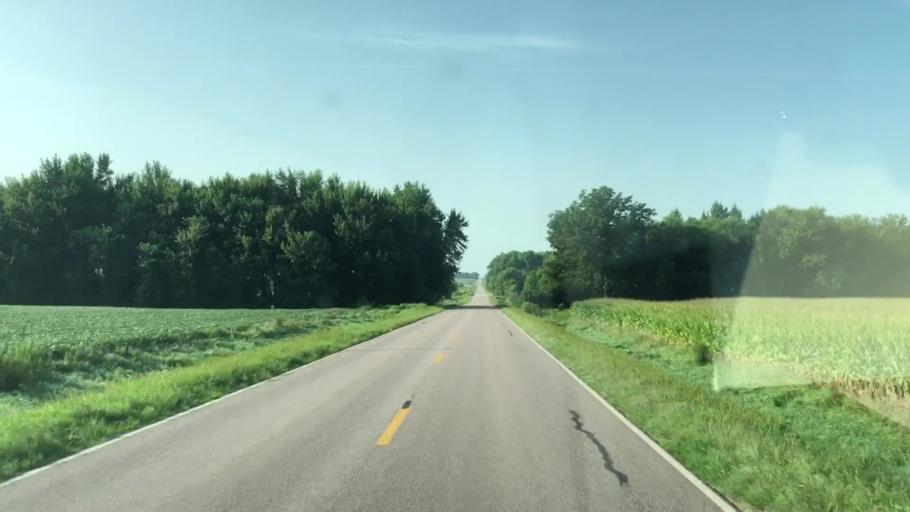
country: US
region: Iowa
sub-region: Lyon County
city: George
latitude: 43.2568
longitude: -96.0002
